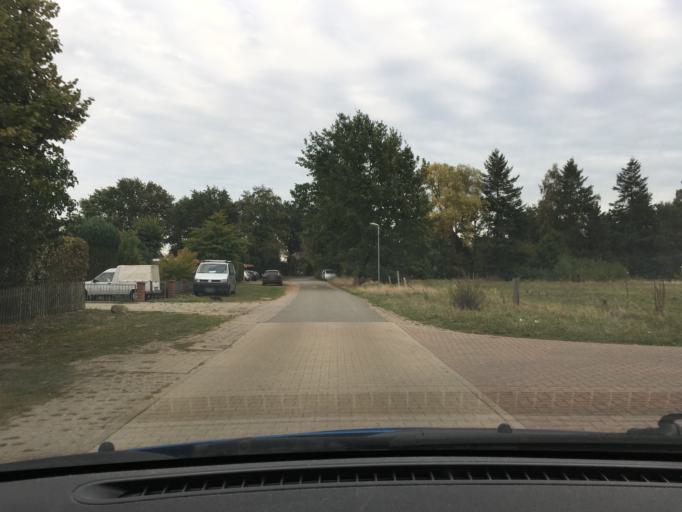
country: DE
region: Lower Saxony
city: Winsen
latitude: 53.3529
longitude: 10.2370
